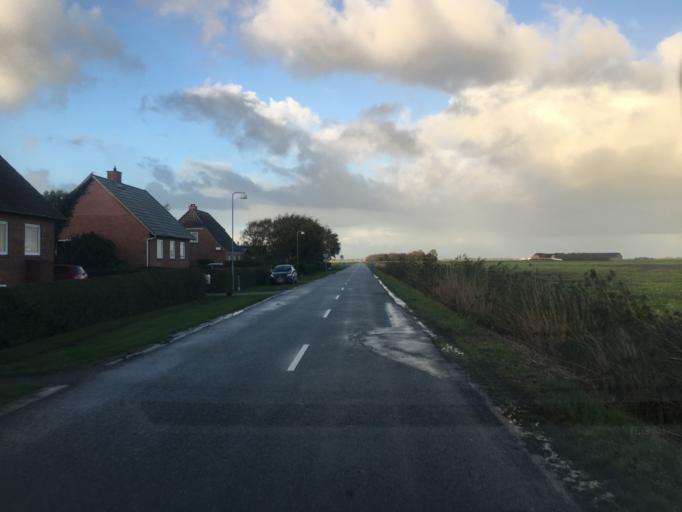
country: DE
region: Schleswig-Holstein
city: Neukirchen
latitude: 54.9027
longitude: 8.7531
